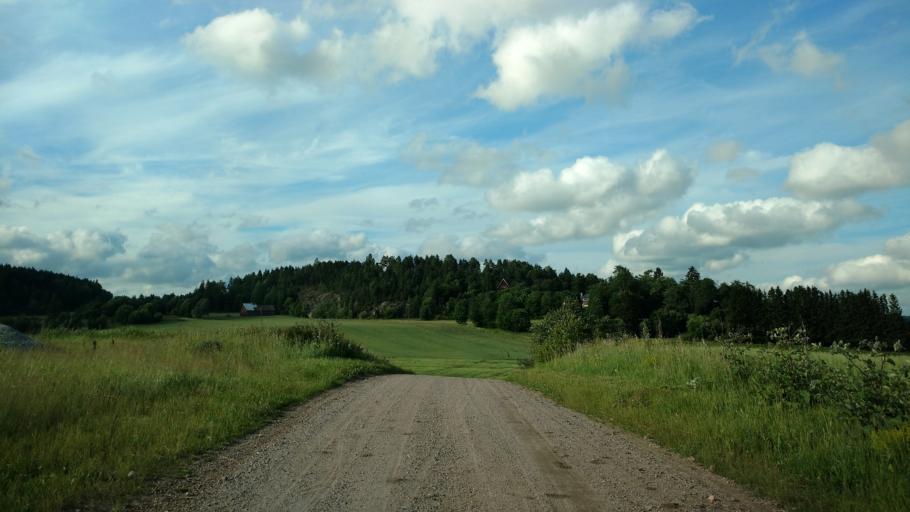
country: FI
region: Varsinais-Suomi
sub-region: Salo
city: Salo
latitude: 60.4218
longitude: 23.1747
